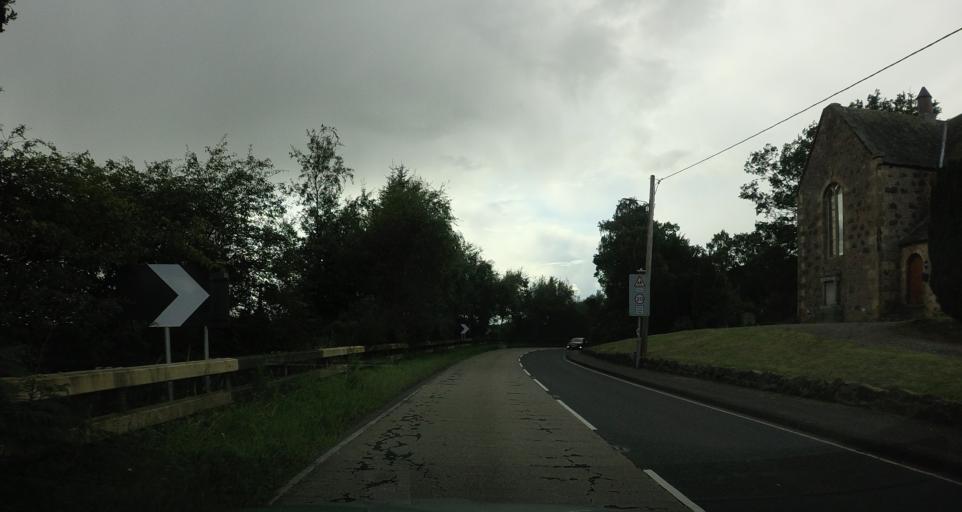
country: GB
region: Scotland
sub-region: Clackmannanshire
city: Dollar
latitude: 56.1544
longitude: -3.6268
